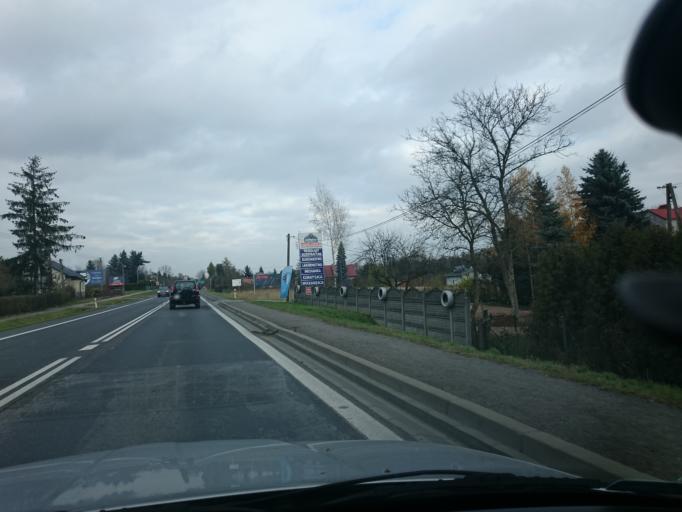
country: PL
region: Lesser Poland Voivodeship
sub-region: Powiat krakowski
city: Michalowice
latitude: 50.1631
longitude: 19.9792
